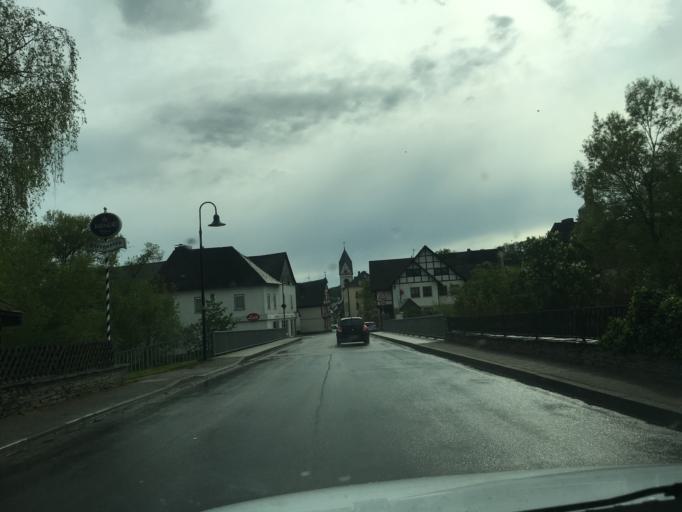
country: DE
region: Rheinland-Pfalz
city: Gemunden
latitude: 49.8958
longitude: 7.4802
